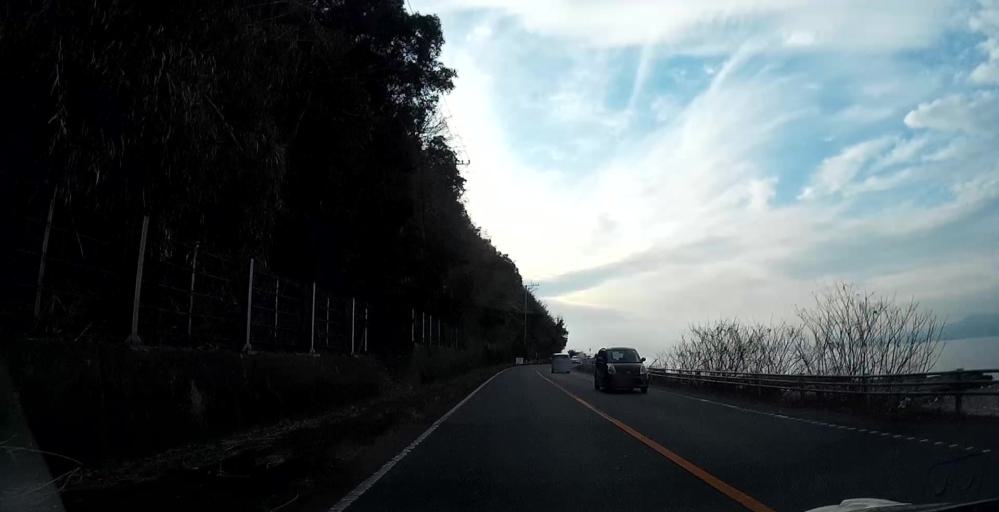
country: JP
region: Nagasaki
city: Shimabara
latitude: 32.6451
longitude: 130.4846
